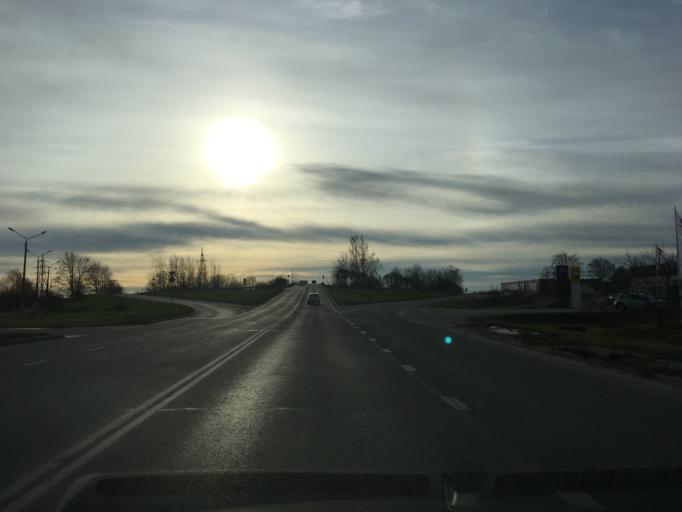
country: EE
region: Ida-Virumaa
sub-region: Narva linn
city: Narva
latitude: 59.3746
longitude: 28.1545
